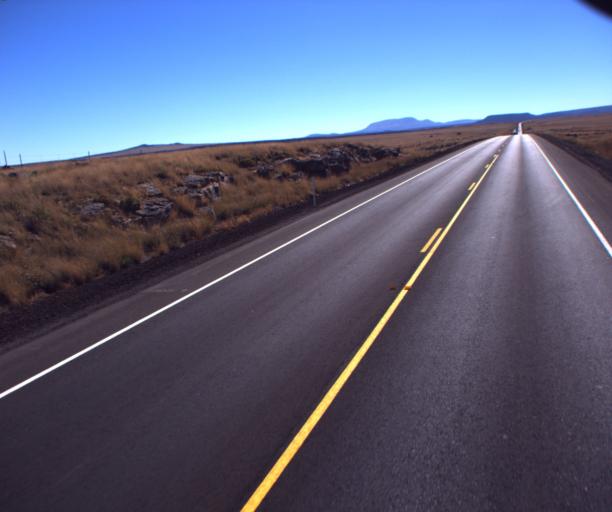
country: US
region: Arizona
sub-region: Apache County
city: Springerville
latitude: 34.2251
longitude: -109.3380
